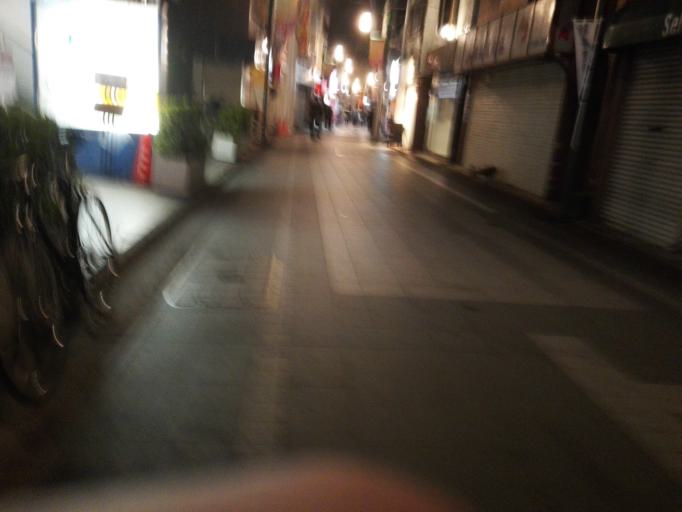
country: JP
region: Tokyo
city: Tokyo
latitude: 35.7107
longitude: 139.6670
